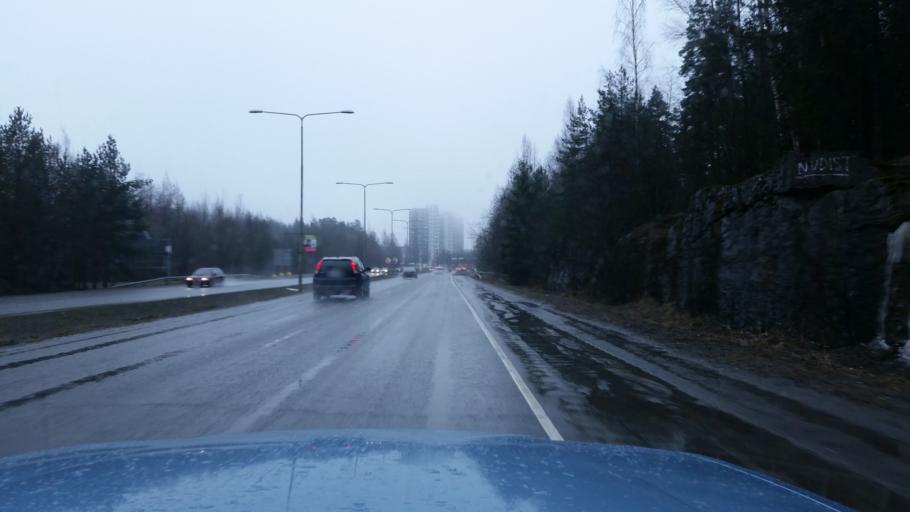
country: FI
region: Pirkanmaa
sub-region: Tampere
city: Tampere
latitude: 61.4625
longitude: 23.8438
